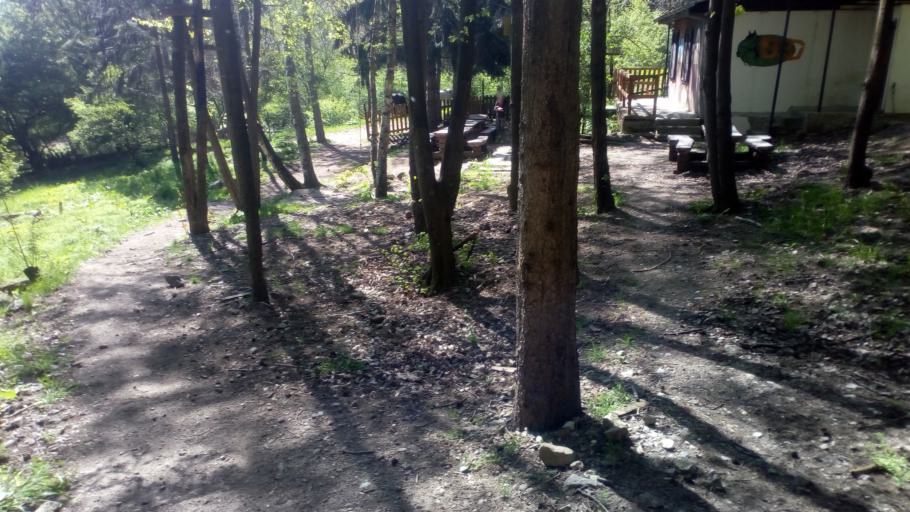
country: BG
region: Sofia-Capital
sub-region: Stolichna Obshtina
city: Sofia
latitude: 42.6208
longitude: 23.3061
